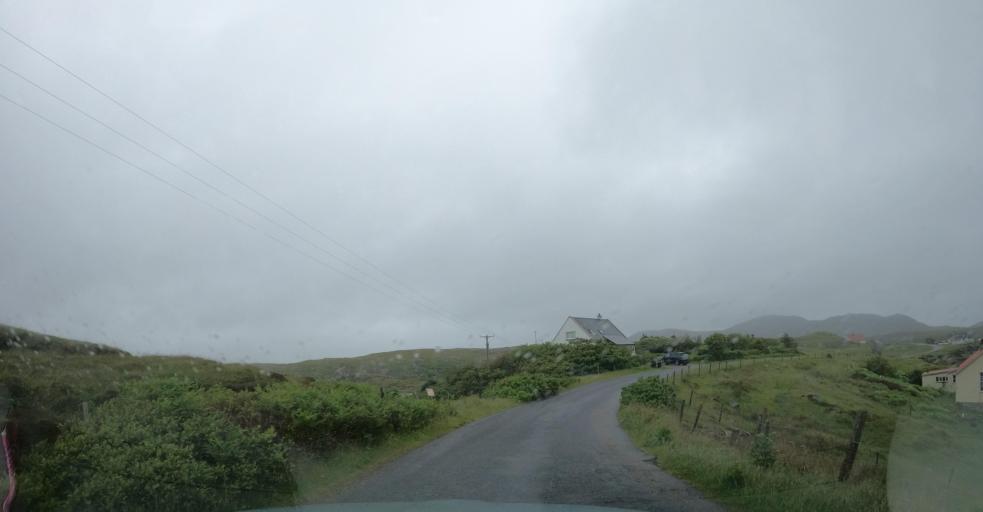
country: GB
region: Scotland
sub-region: Eilean Siar
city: Benbecula
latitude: 57.4795
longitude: -7.2103
